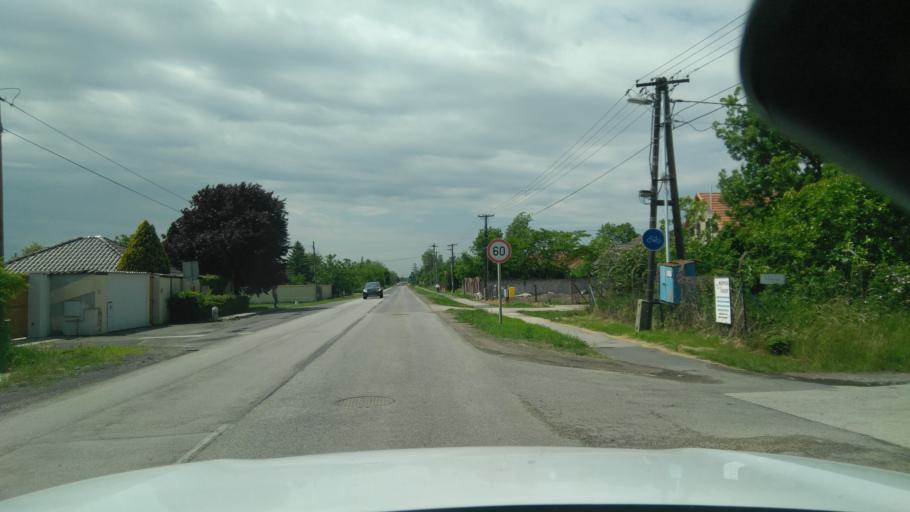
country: HU
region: Bekes
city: Bekescsaba
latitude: 46.6947
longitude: 21.1316
